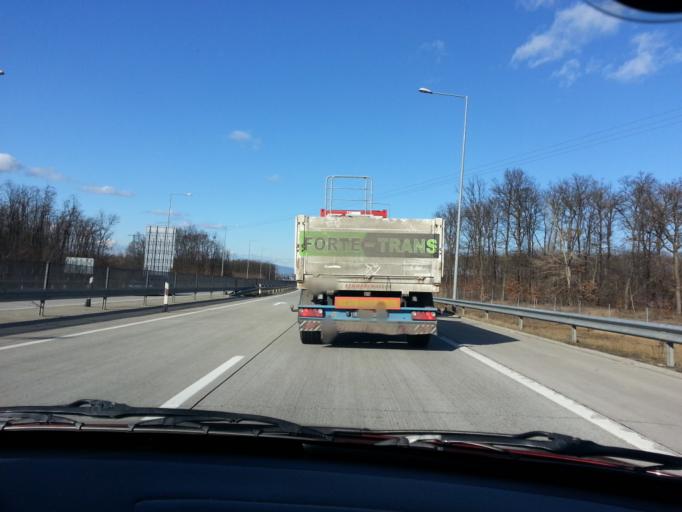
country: HU
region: Pest
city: Szada
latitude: 47.6060
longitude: 19.3201
